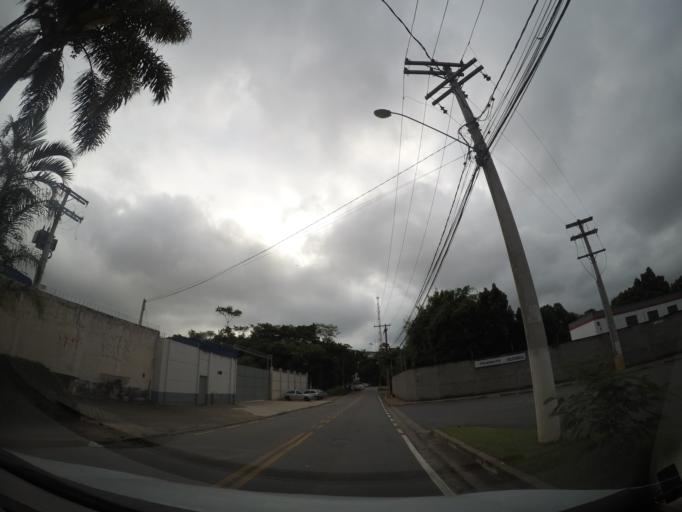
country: BR
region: Sao Paulo
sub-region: Aruja
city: Aruja
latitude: -23.4035
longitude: -46.3473
